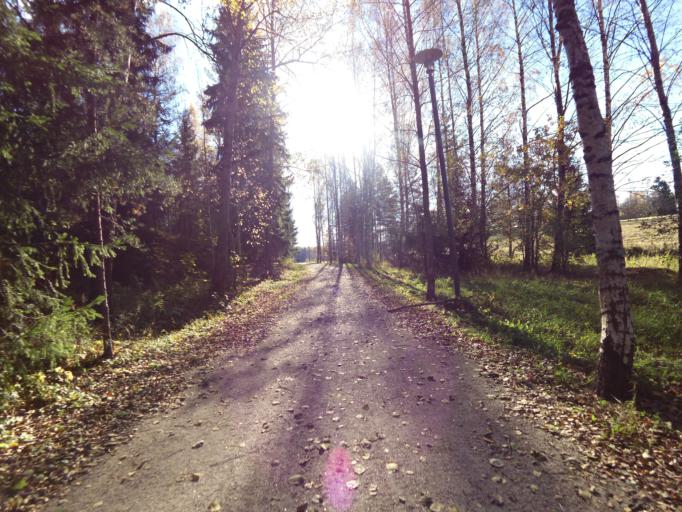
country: FI
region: Uusimaa
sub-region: Helsinki
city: Espoo
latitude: 60.1928
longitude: 24.6745
